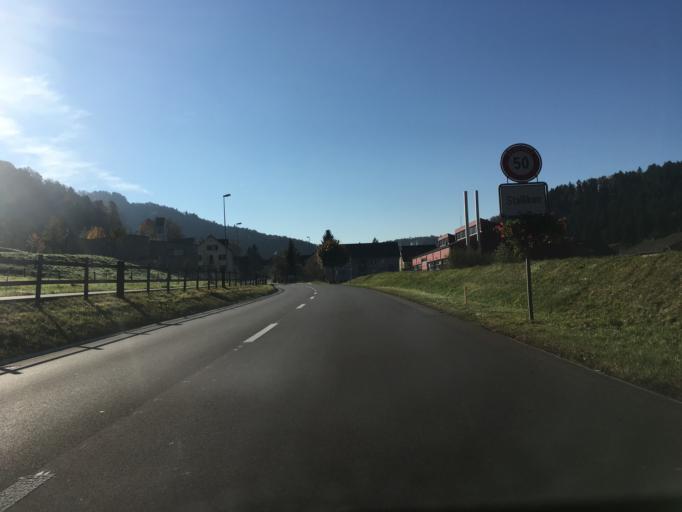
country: CH
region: Zurich
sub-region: Bezirk Affoltern
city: Wettswil / Ausser-Dorf
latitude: 47.3293
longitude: 8.4893
